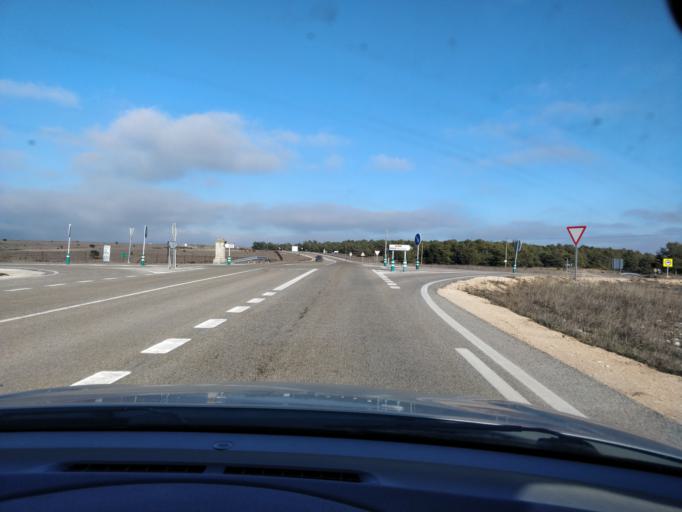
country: ES
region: Castille and Leon
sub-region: Provincia de Burgos
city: Abajas
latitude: 42.6520
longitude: -3.6239
